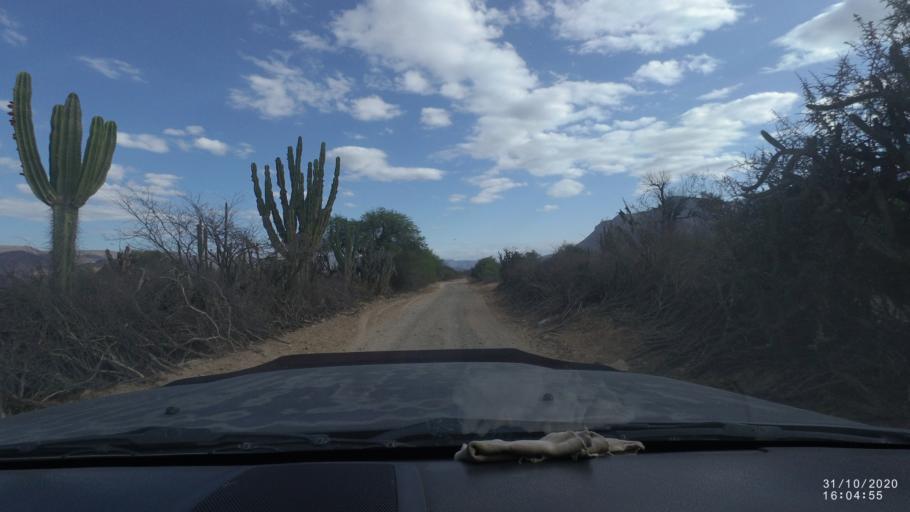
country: BO
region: Chuquisaca
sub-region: Provincia Zudanez
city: Mojocoya
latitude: -18.3630
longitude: -64.6500
